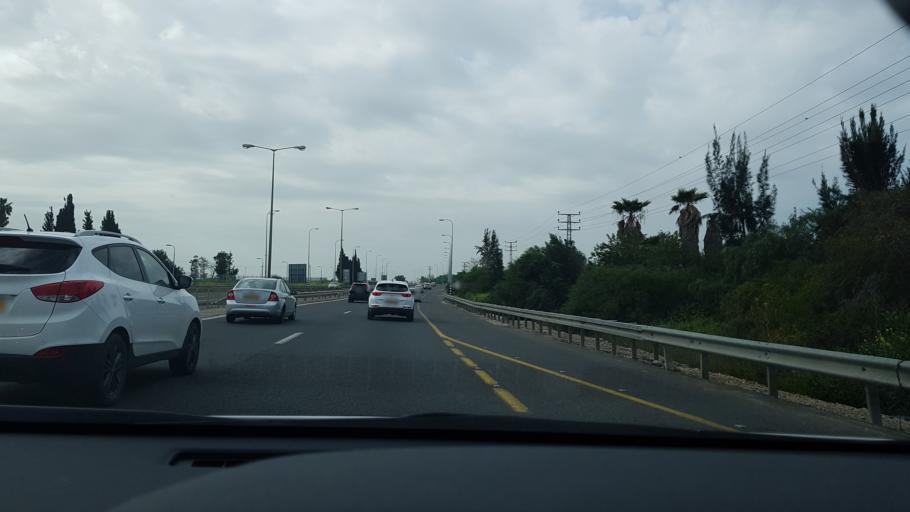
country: IL
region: Southern District
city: Ashqelon
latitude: 31.6741
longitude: 34.6089
